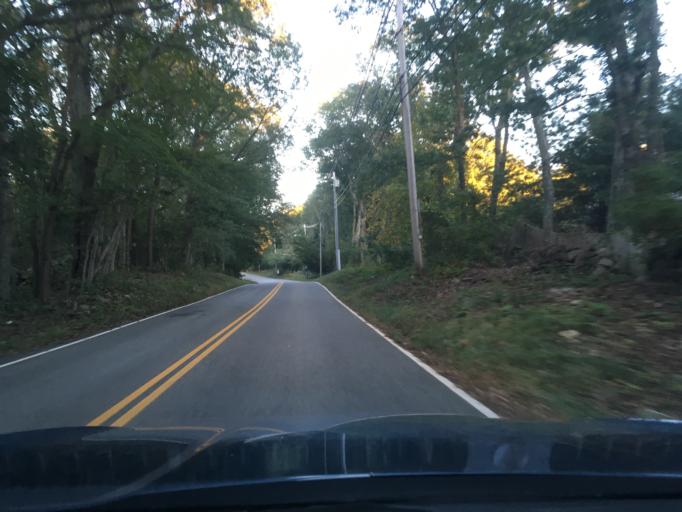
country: US
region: Rhode Island
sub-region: Kent County
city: West Warwick
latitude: 41.6428
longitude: -71.5232
